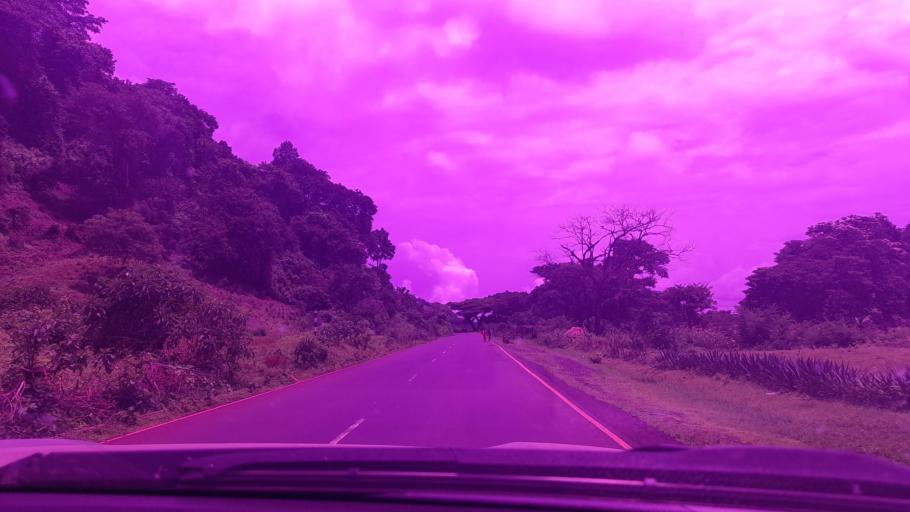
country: ET
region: Oromiya
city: Metu
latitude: 8.3344
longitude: 35.7458
